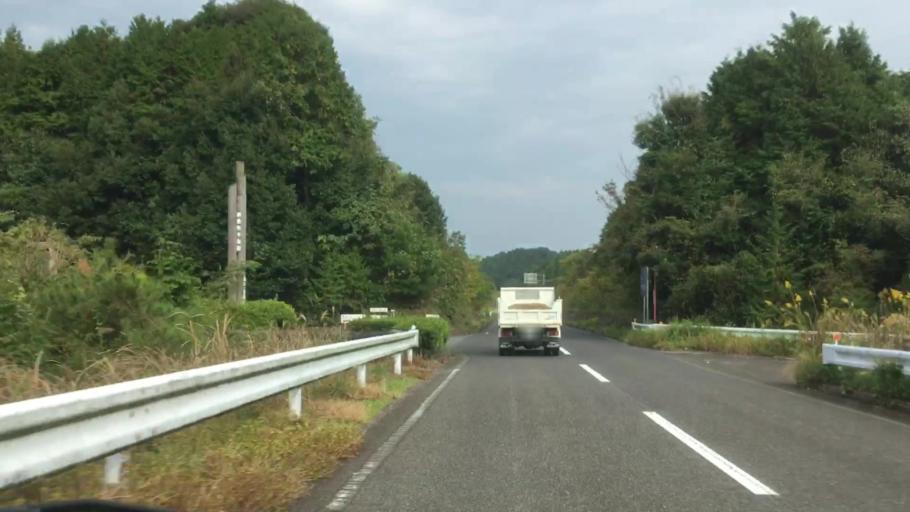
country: JP
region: Nagasaki
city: Sasebo
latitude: 33.0201
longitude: 129.6996
